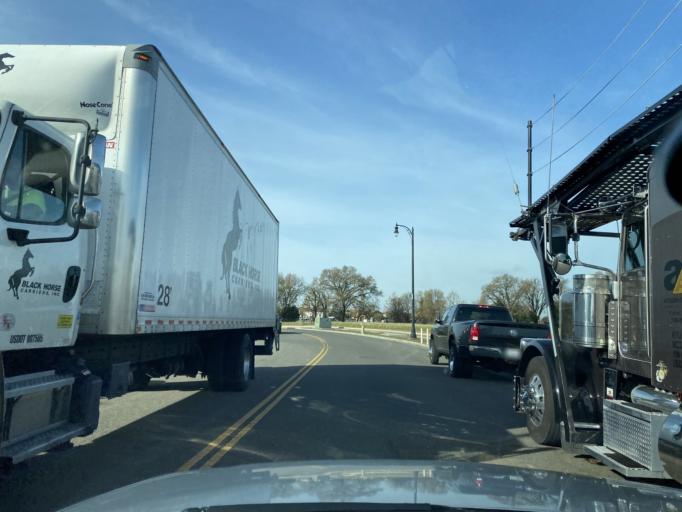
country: US
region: California
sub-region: Sacramento County
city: Elk Grove
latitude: 38.4039
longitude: -121.3934
